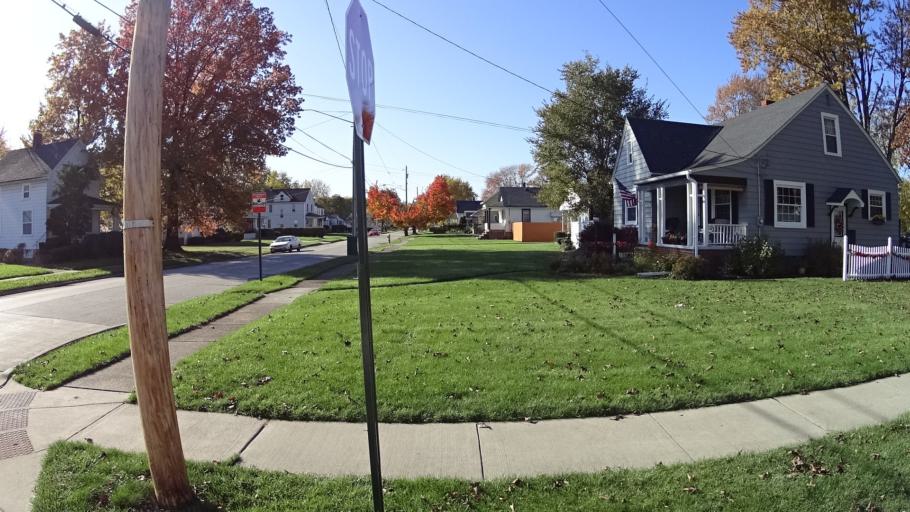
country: US
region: Ohio
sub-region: Lorain County
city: Lorain
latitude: 41.4501
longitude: -82.1887
